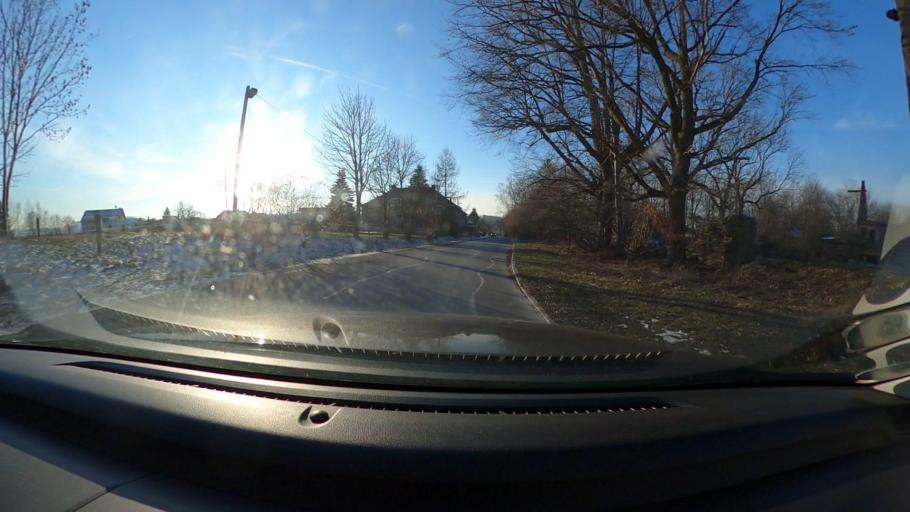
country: DE
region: Saxony
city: Frankenstein
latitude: 50.9371
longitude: 13.2181
